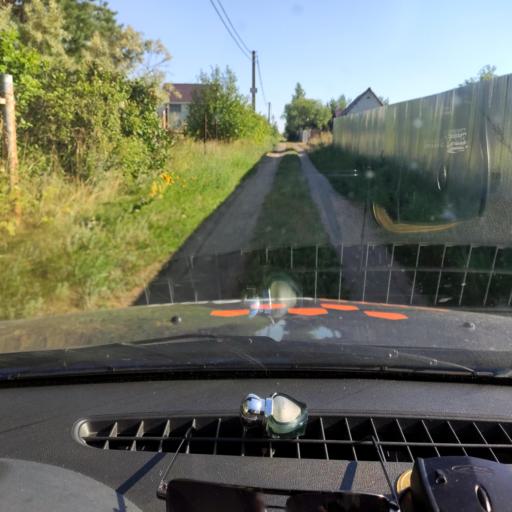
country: RU
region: Voronezj
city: Podgornoye
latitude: 51.8644
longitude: 39.1771
